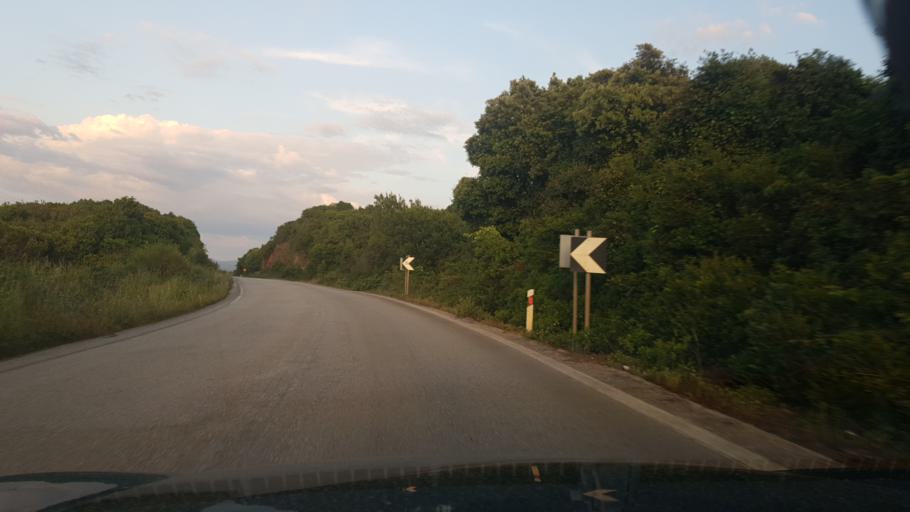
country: GR
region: Ionian Islands
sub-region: Lefkada
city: Lefkada
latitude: 38.8636
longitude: 20.7786
